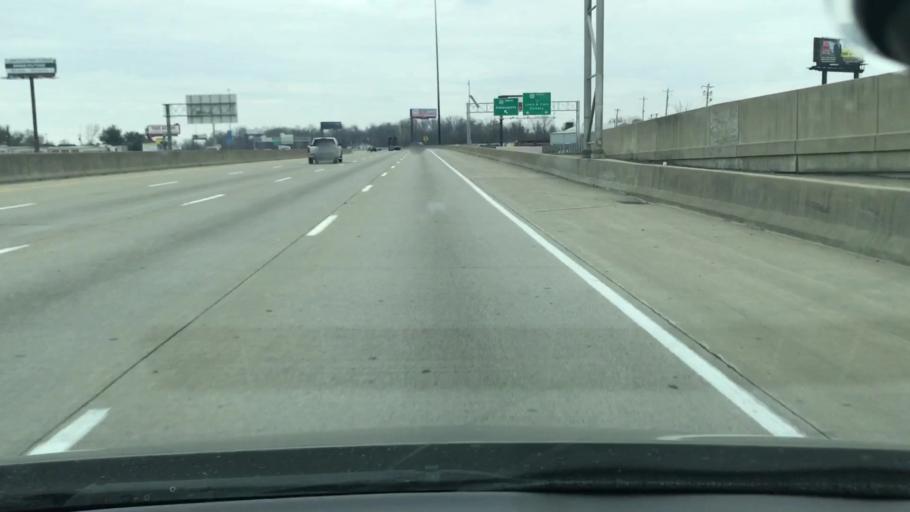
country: US
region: Indiana
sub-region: Clark County
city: Clarksville
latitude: 38.2961
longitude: -85.7557
